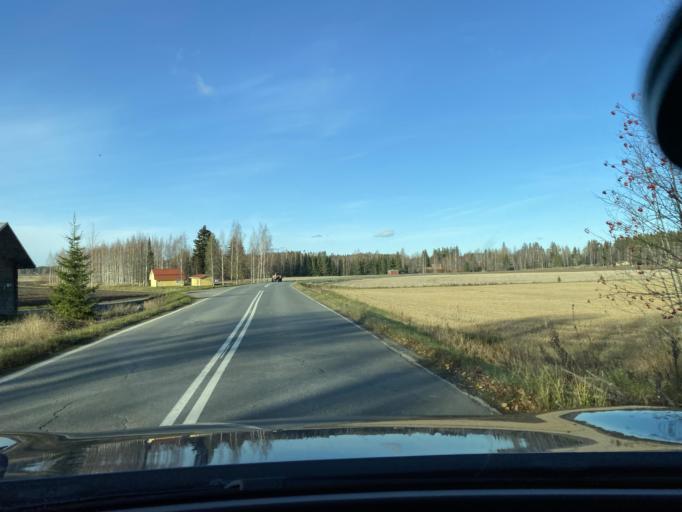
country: FI
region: Haeme
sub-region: Forssa
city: Tammela
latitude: 60.8389
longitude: 23.8349
